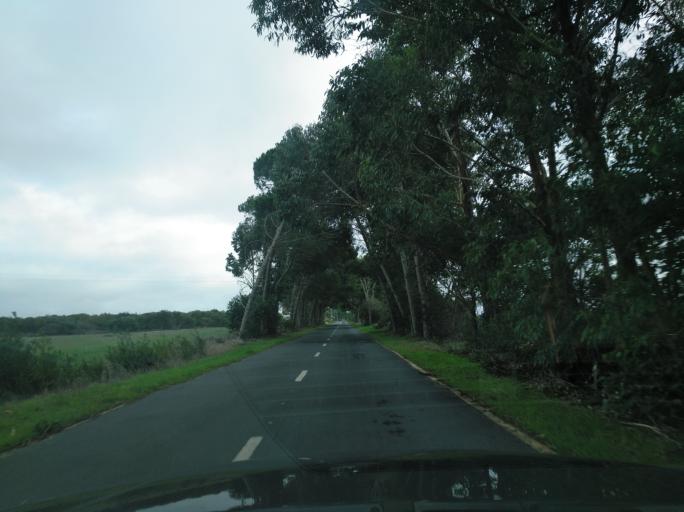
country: PT
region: Beja
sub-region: Odemira
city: Vila Nova de Milfontes
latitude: 37.7087
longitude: -8.7753
